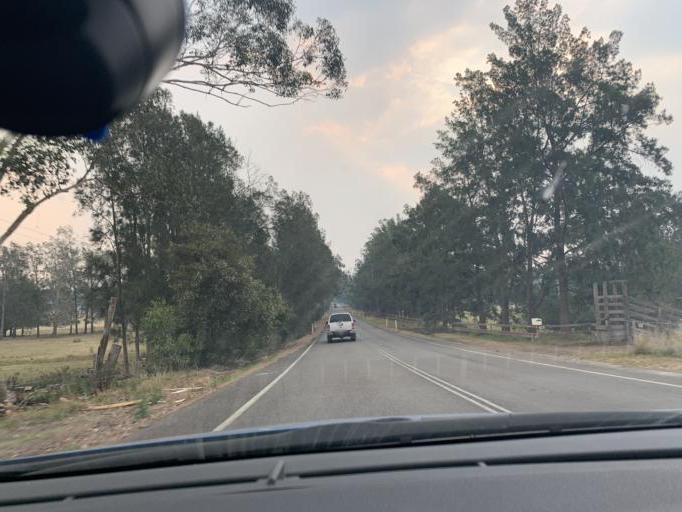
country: AU
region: New South Wales
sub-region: Cessnock
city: Cessnock
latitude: -32.9210
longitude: 151.3473
